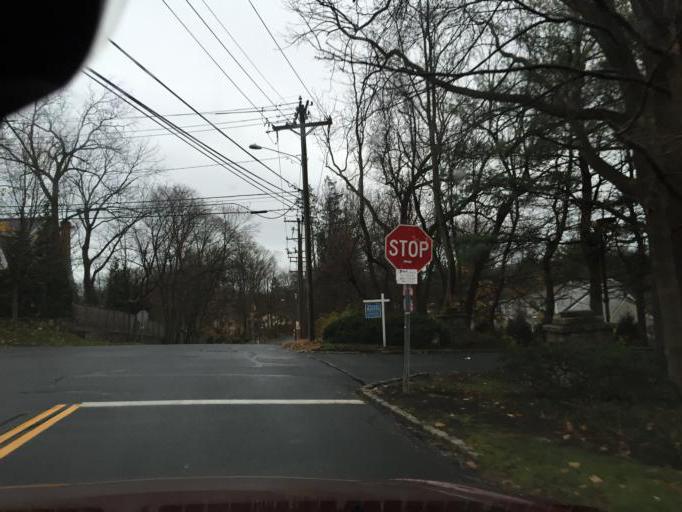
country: US
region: Connecticut
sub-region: Fairfield County
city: Westport
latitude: 41.1253
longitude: -73.3793
